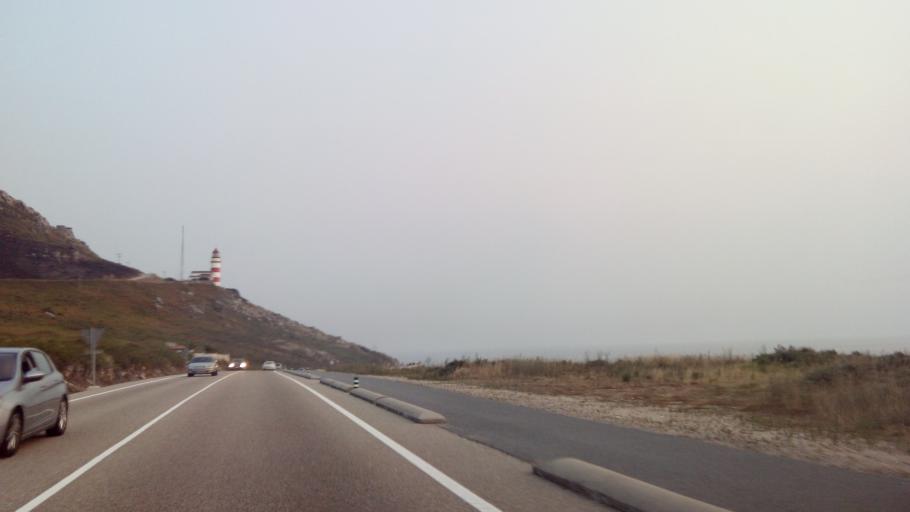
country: ES
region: Galicia
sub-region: Provincia de Pontevedra
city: Baiona
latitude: 42.1091
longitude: -8.8969
